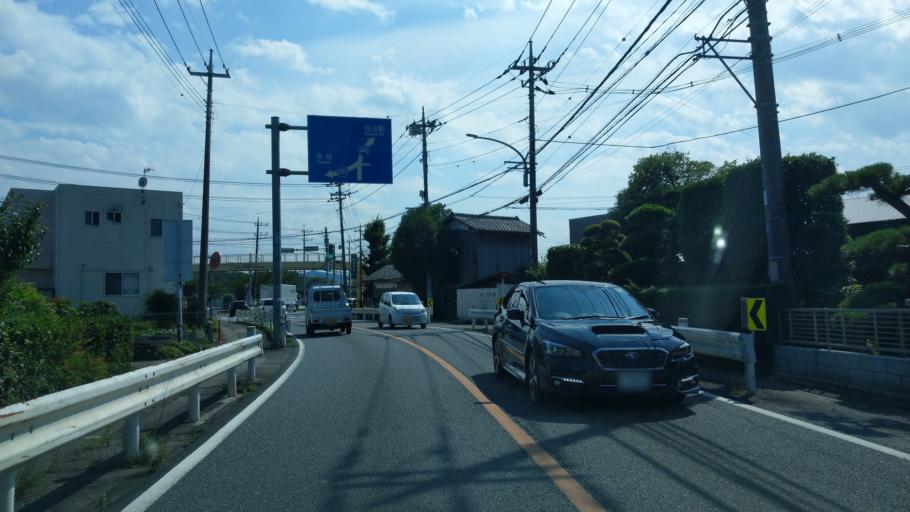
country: JP
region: Saitama
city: Kodamacho-kodamaminami
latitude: 36.2105
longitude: 139.1512
